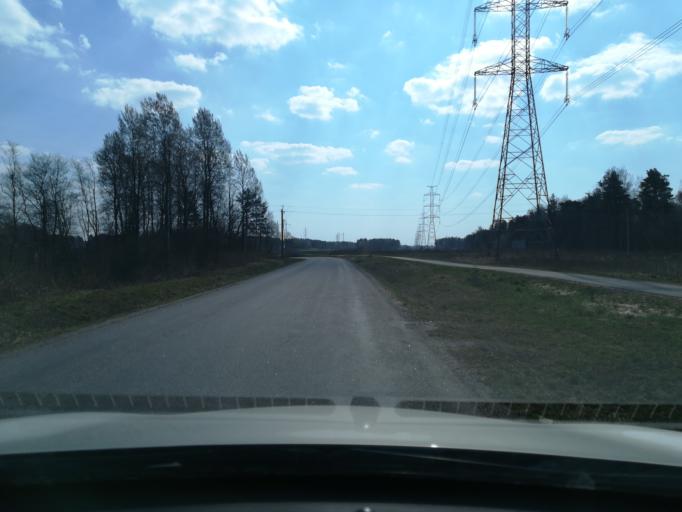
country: EE
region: Harju
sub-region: Saue vald
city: Laagri
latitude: 59.3512
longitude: 24.5916
